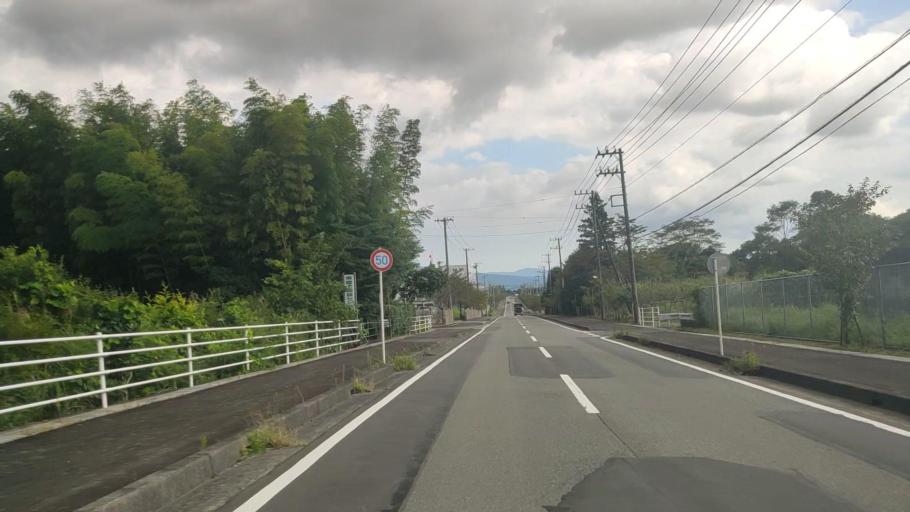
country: JP
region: Shizuoka
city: Gotemba
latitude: 35.2750
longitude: 138.8928
